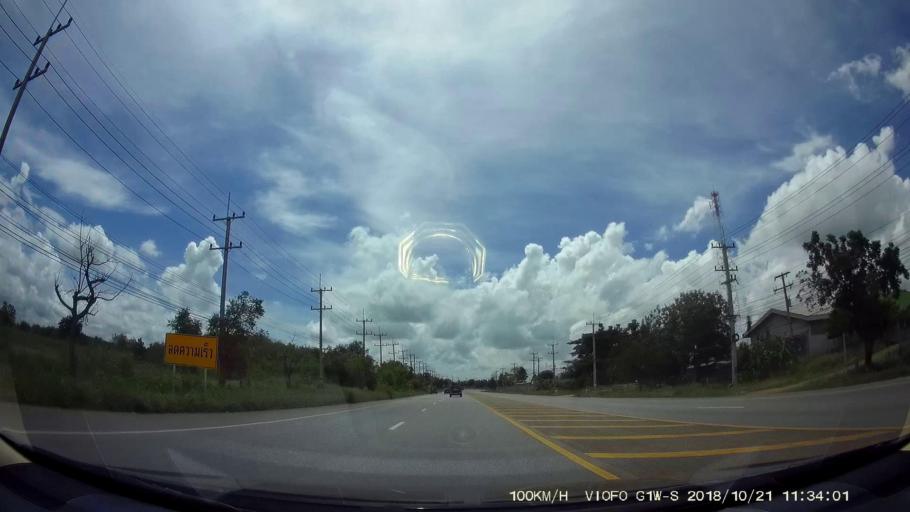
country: TH
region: Chaiyaphum
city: Chaiyaphum
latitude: 15.7374
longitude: 102.0244
